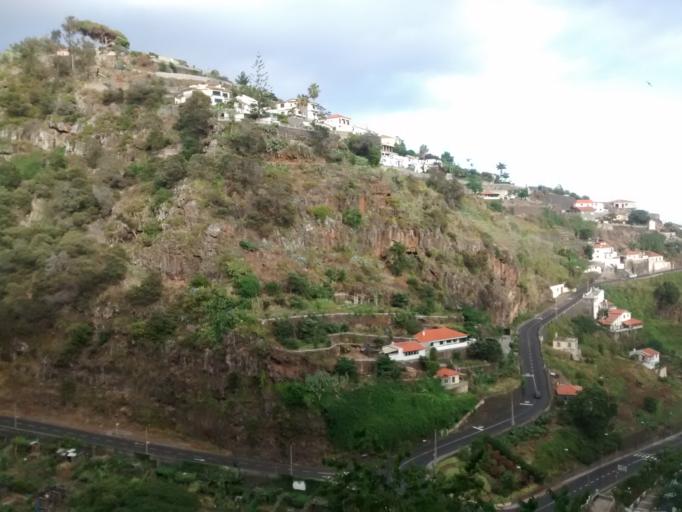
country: PT
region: Madeira
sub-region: Funchal
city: Nossa Senhora do Monte
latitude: 32.6613
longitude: -16.9013
